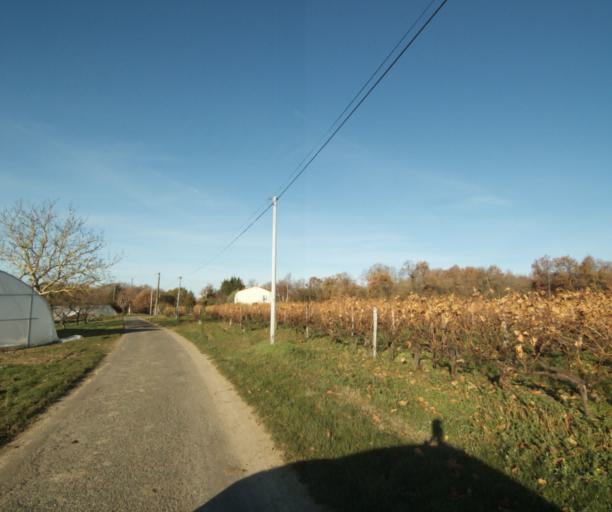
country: FR
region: Poitou-Charentes
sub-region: Departement de la Charente-Maritime
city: Cherac
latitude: 45.7078
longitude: -0.4539
